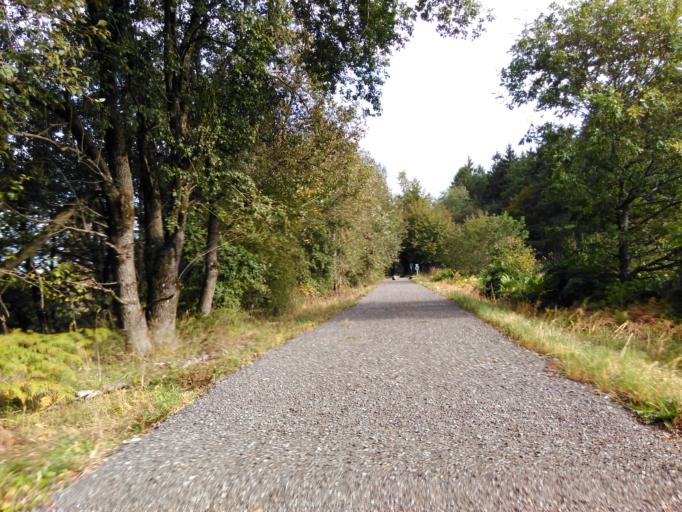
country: BE
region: Wallonia
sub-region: Province du Luxembourg
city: Vaux-sur-Sure
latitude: 49.9282
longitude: 5.5131
